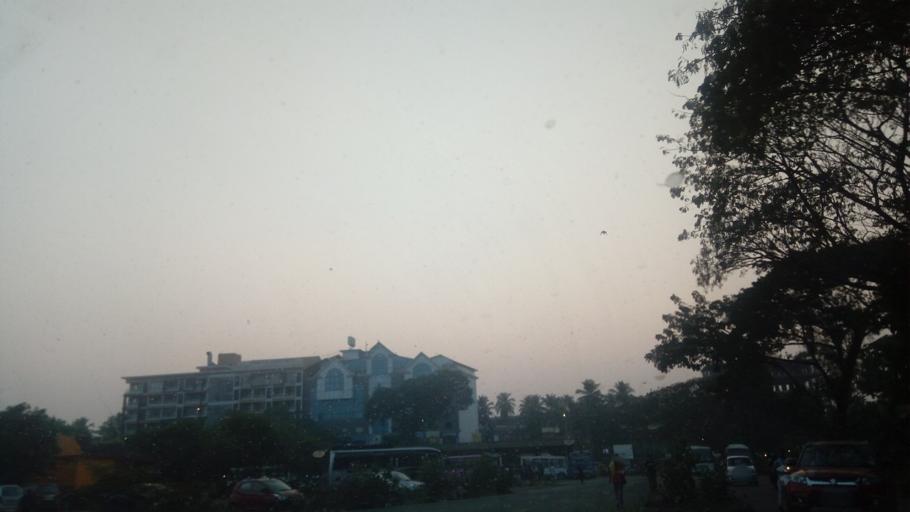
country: IN
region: Goa
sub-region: South Goa
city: Madgaon
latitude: 15.2884
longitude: 73.9562
